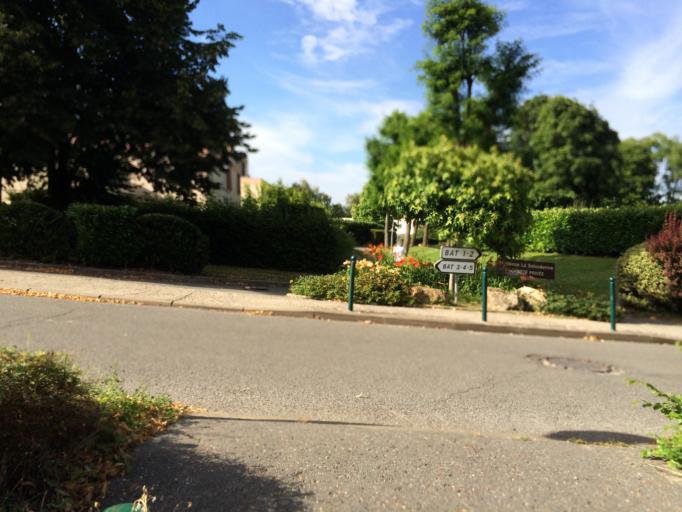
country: FR
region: Ile-de-France
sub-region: Departement de l'Essonne
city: Saulx-les-Chartreux
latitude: 48.6922
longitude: 2.2737
